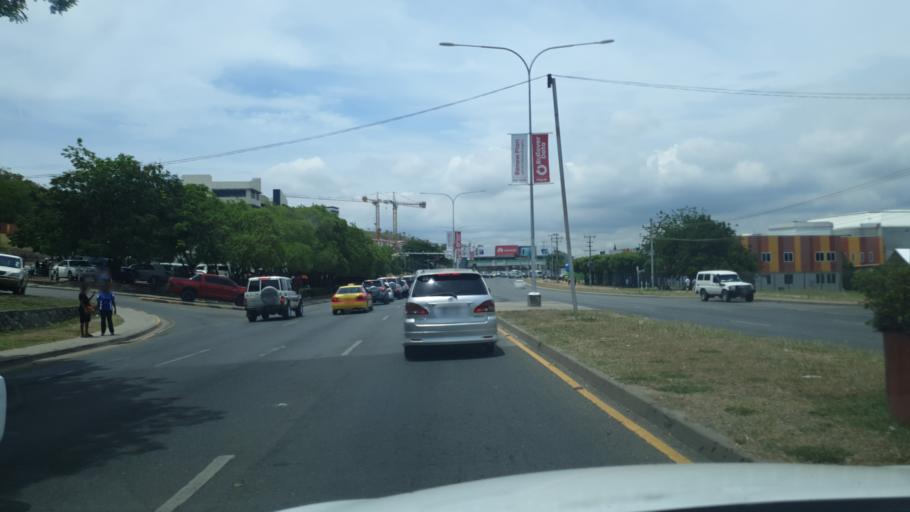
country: PG
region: National Capital
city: Port Moresby
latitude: -9.4418
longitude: 147.1814
